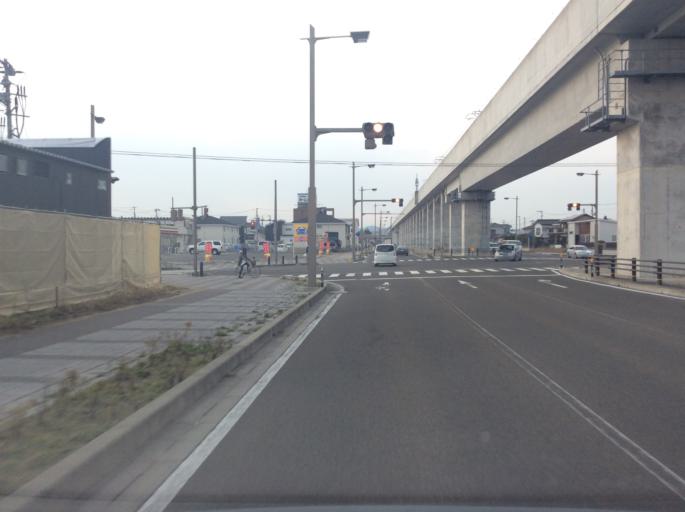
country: JP
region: Miyagi
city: Iwanuma
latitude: 38.1611
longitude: 140.9119
